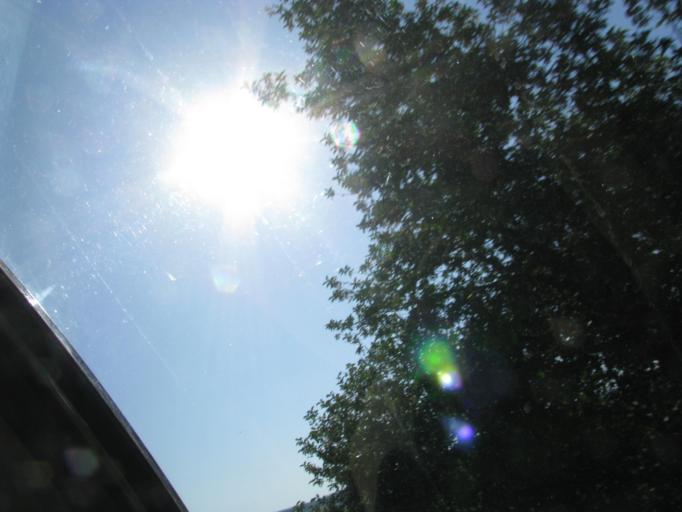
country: US
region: Washington
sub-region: Spokane County
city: Liberty Lake
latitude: 47.6334
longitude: -117.1196
